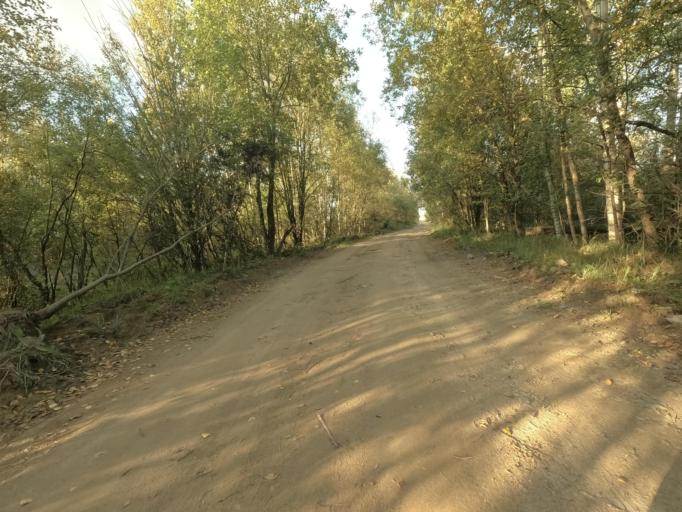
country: RU
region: Leningrad
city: Imeni Sverdlova
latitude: 59.8574
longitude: 30.7323
